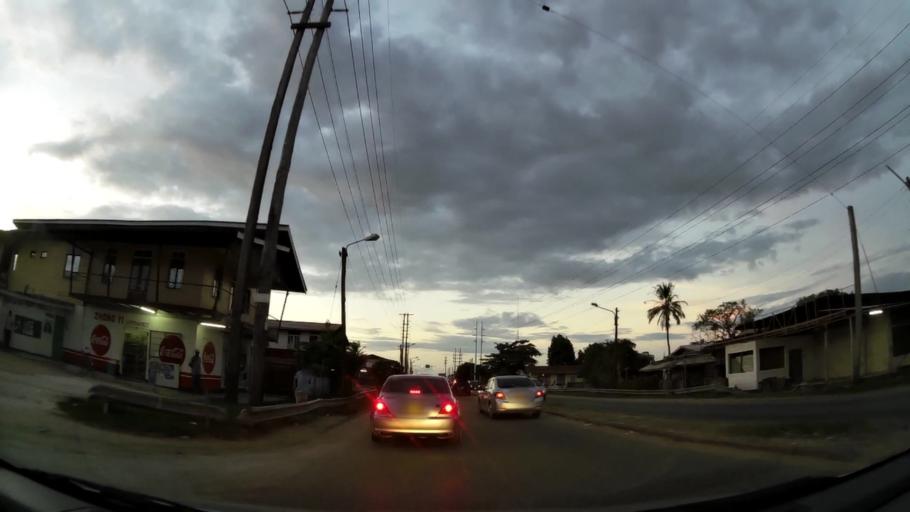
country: SR
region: Paramaribo
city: Paramaribo
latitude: 5.7960
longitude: -55.1769
